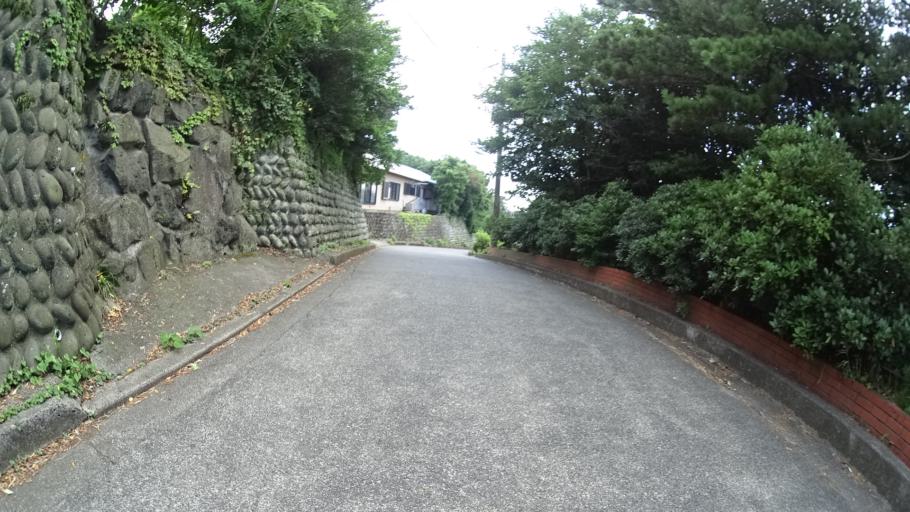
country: JP
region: Shizuoka
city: Shimoda
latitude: 34.5286
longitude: 139.2795
